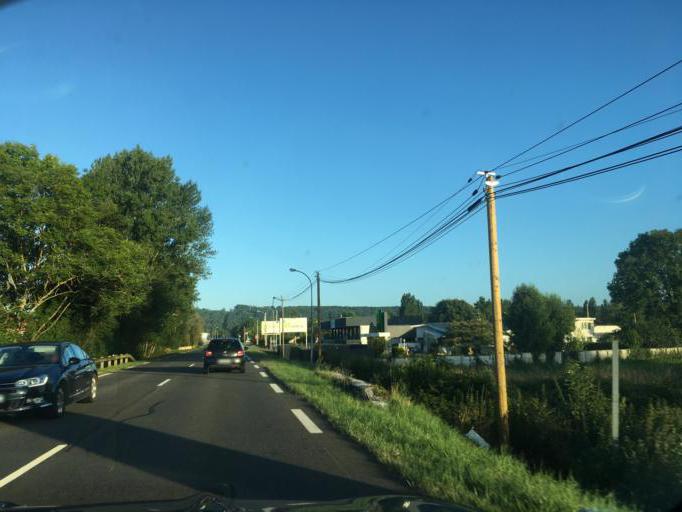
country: FR
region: Midi-Pyrenees
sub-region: Departement des Hautes-Pyrenees
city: Ibos
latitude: 43.2421
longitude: 0.0017
